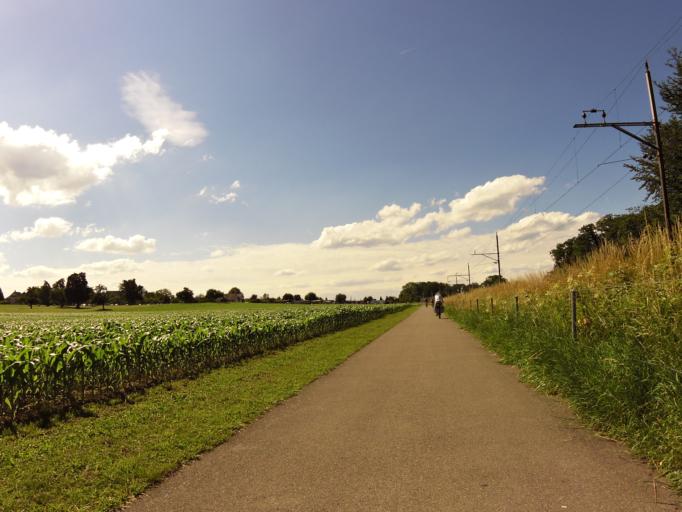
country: CH
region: Thurgau
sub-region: Arbon District
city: Egnach
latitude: 47.5348
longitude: 9.4040
